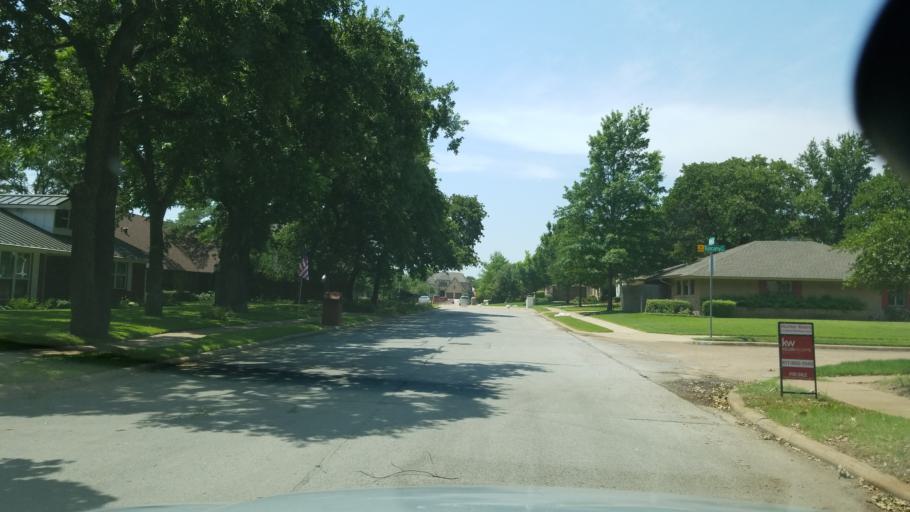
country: US
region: Texas
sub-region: Dallas County
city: Irving
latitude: 32.8501
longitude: -96.9436
